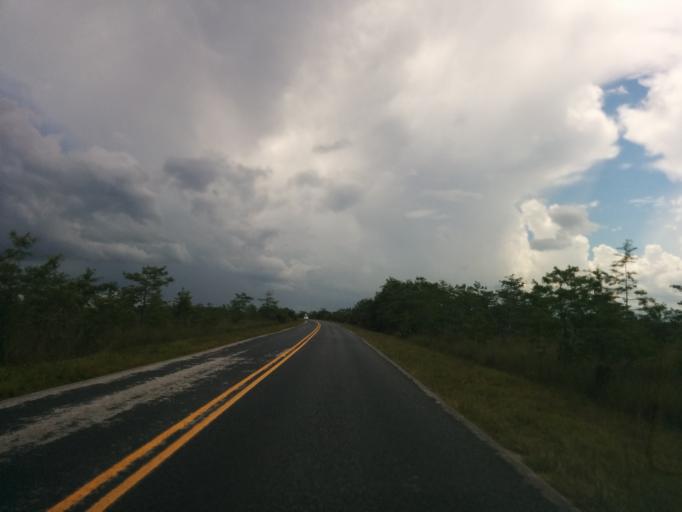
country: US
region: Florida
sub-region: Miami-Dade County
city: Florida City
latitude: 25.4323
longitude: -80.7621
